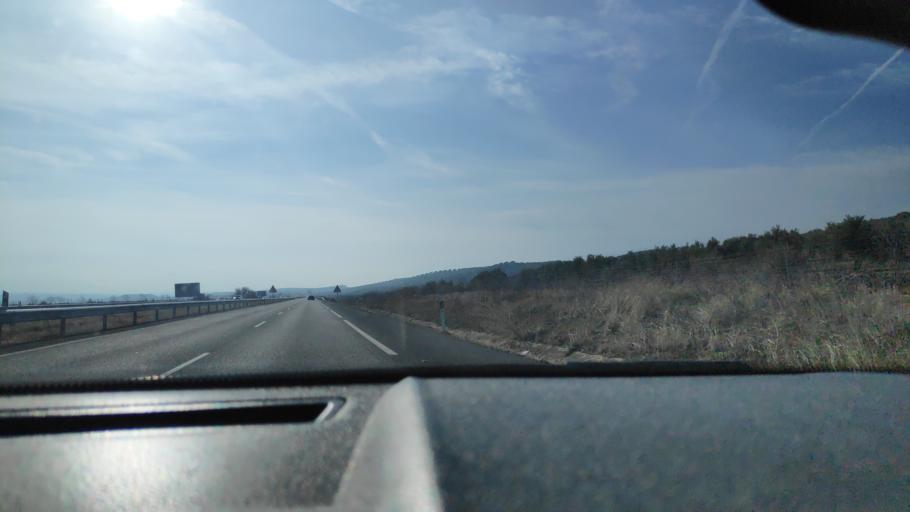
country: ES
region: Andalusia
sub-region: Provincia de Jaen
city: Mengibar
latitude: 37.8991
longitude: -3.7814
